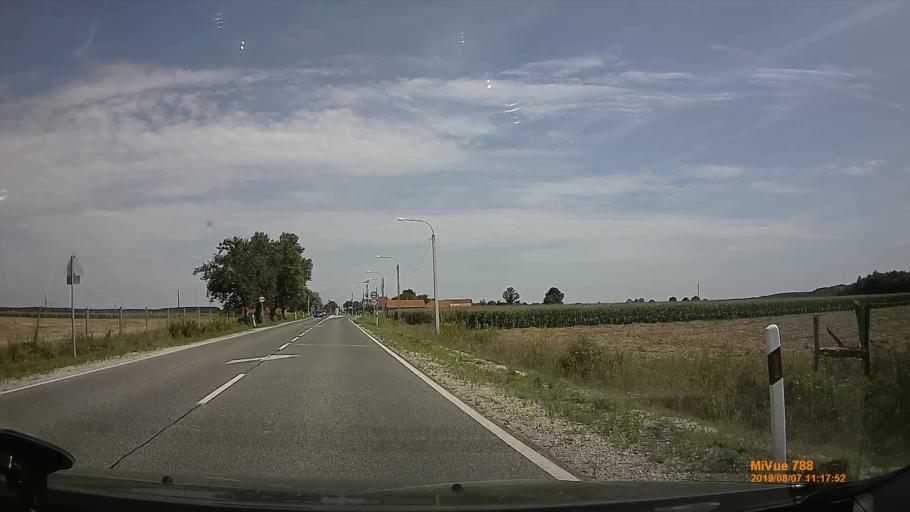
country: HU
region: Zala
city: Zalalovo
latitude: 46.7483
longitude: 16.5572
